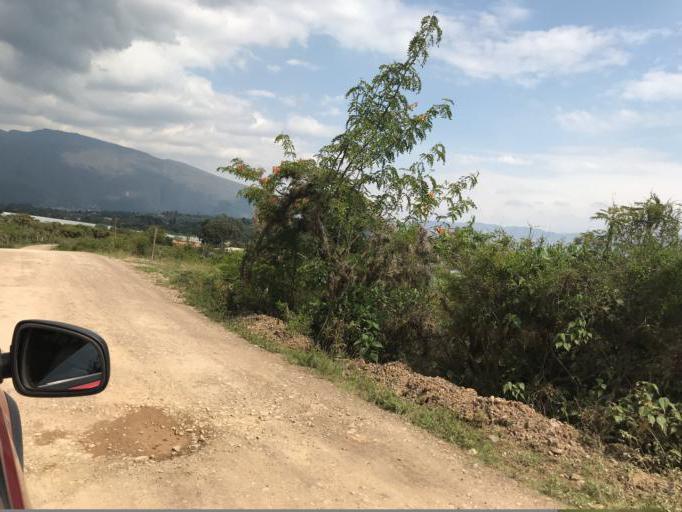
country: CO
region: Boyaca
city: Villa de Leiva
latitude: 5.6483
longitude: -73.5641
